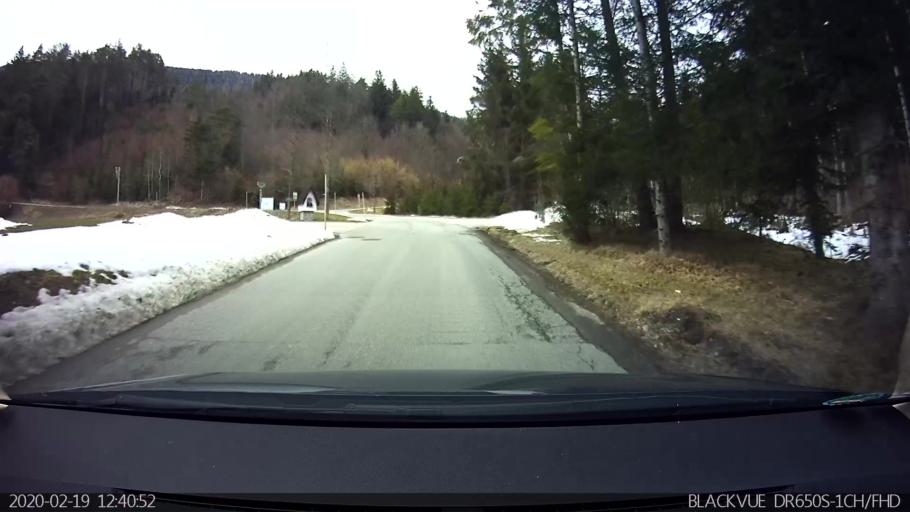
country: AT
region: Tyrol
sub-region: Politischer Bezirk Schwaz
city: Terfens
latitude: 47.3275
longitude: 11.6335
